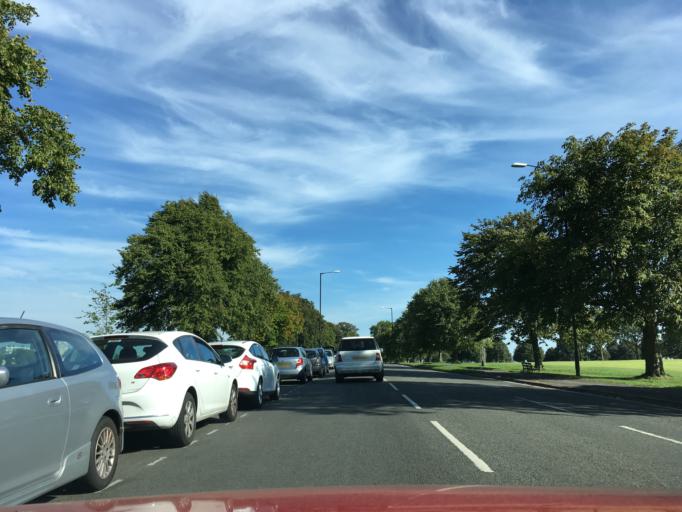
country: GB
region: England
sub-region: Bristol
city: Bristol
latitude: 51.4742
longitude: -2.6238
